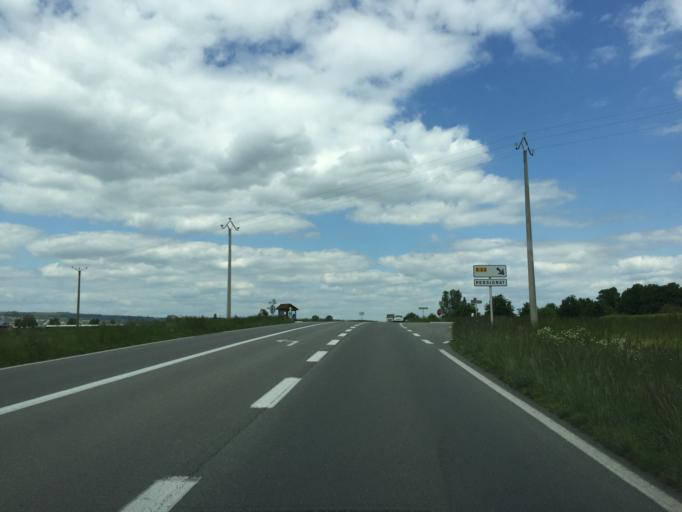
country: FR
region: Auvergne
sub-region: Departement du Puy-de-Dome
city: Aigueperse
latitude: 45.9749
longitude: 3.1799
